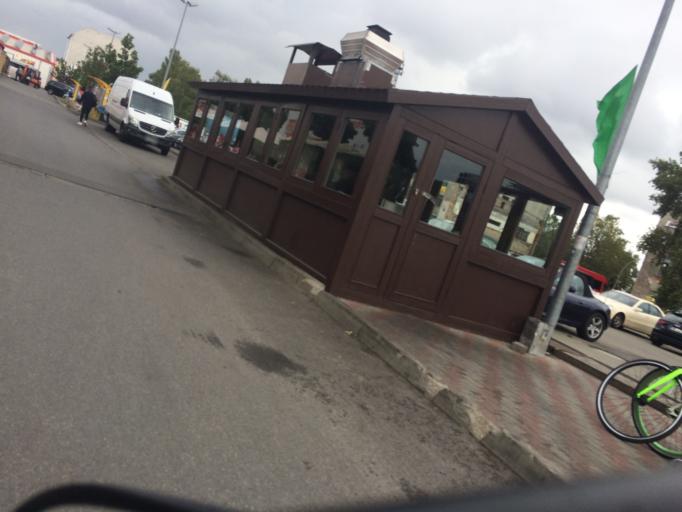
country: DE
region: Berlin
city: Fennpfuhl
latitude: 52.5276
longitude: 13.4890
